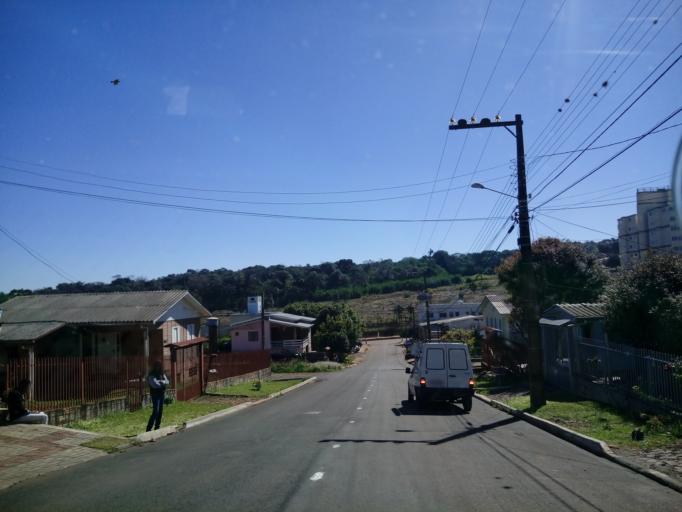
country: BR
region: Santa Catarina
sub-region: Chapeco
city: Chapeco
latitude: -27.0967
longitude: -52.6777
